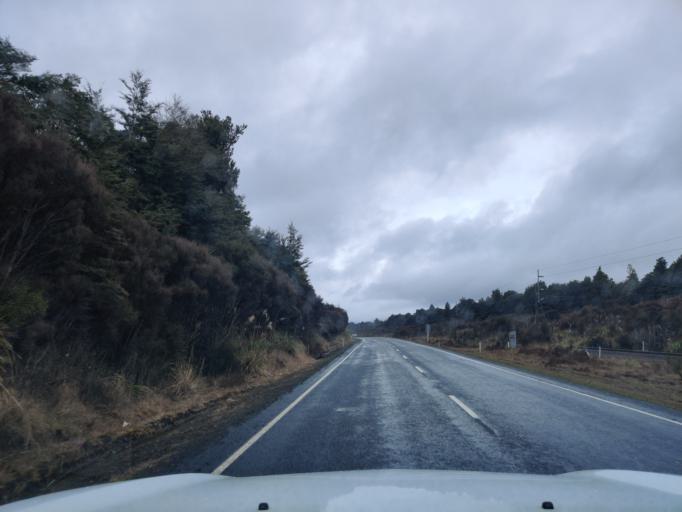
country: NZ
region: Manawatu-Wanganui
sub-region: Ruapehu District
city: Waiouru
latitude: -39.3096
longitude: 175.3893
